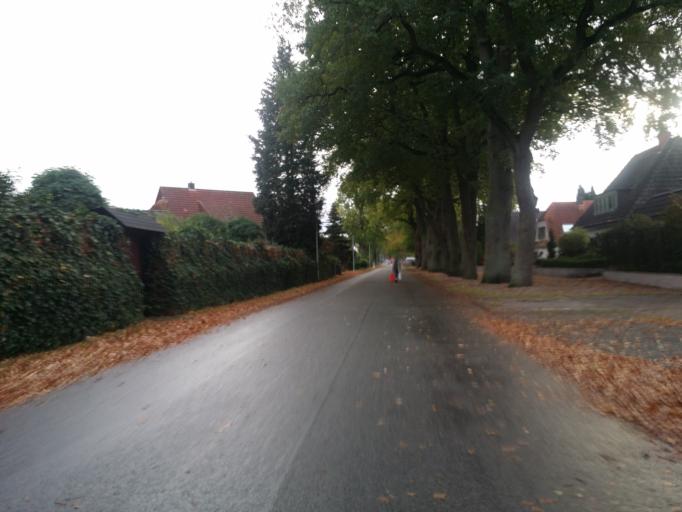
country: DE
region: Lower Saxony
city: Stuhr
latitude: 53.0393
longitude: 8.7210
